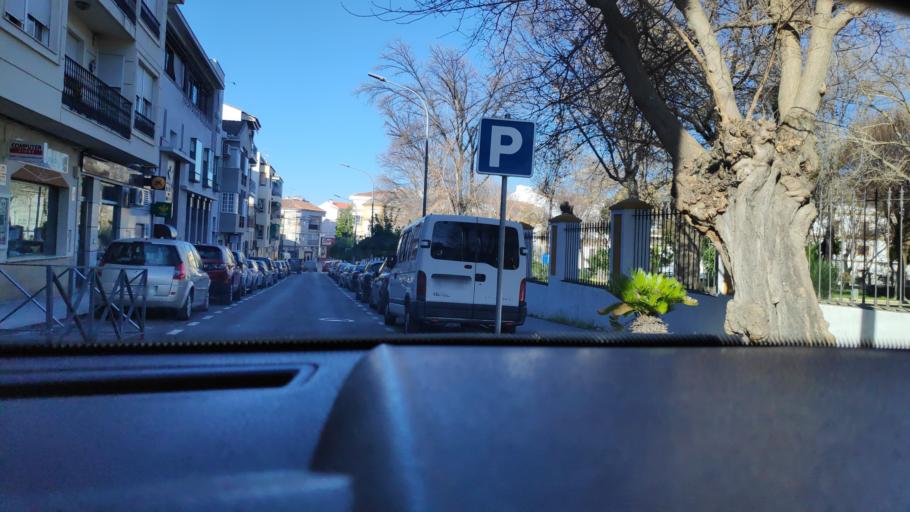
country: ES
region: Andalusia
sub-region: Province of Cordoba
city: Baena
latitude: 37.6163
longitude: -4.3213
